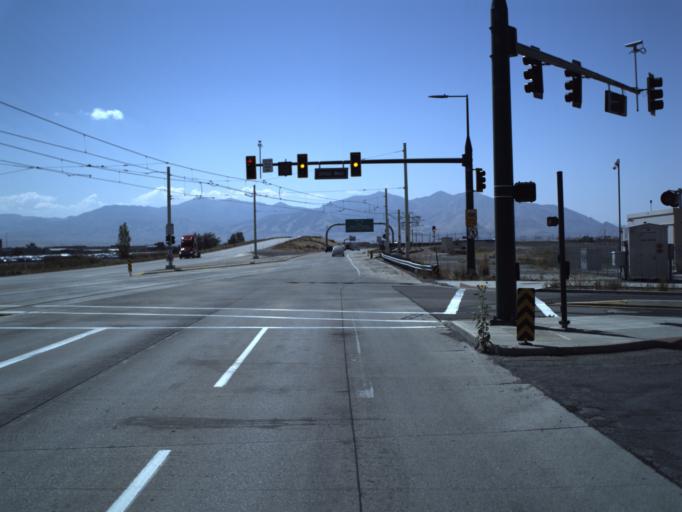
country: US
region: Utah
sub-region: Salt Lake County
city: Salt Lake City
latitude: 40.7684
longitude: -111.9578
